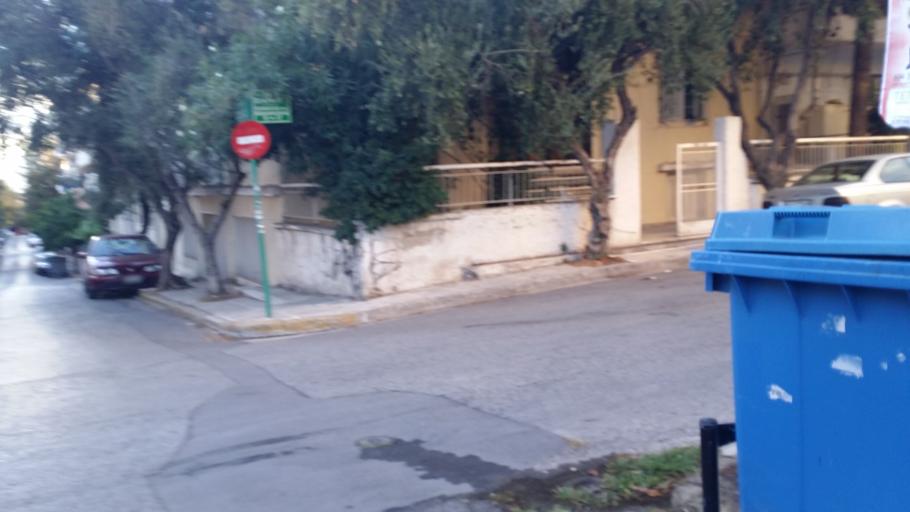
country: GR
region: Attica
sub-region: Nomarchia Athinas
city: Irakleio
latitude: 38.0501
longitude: 23.7588
